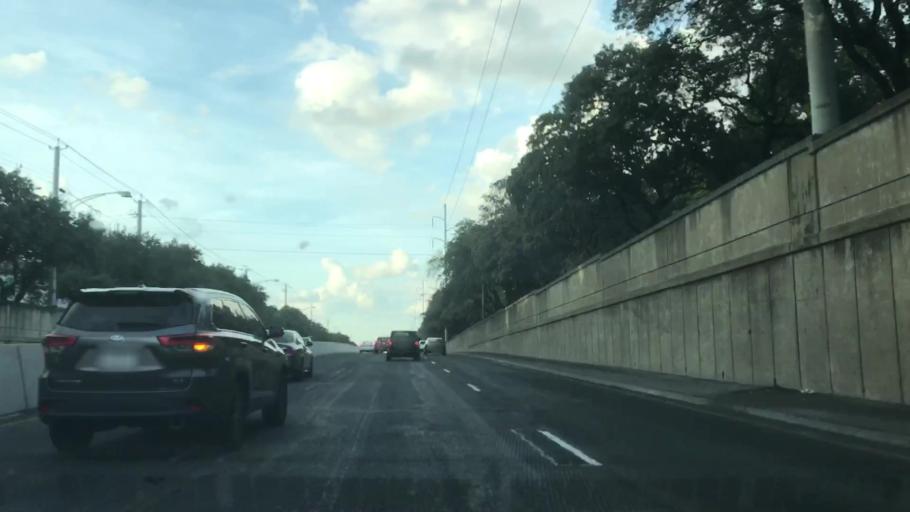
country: US
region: Texas
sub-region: Dallas County
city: Highland Park
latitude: 32.8284
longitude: -96.8159
